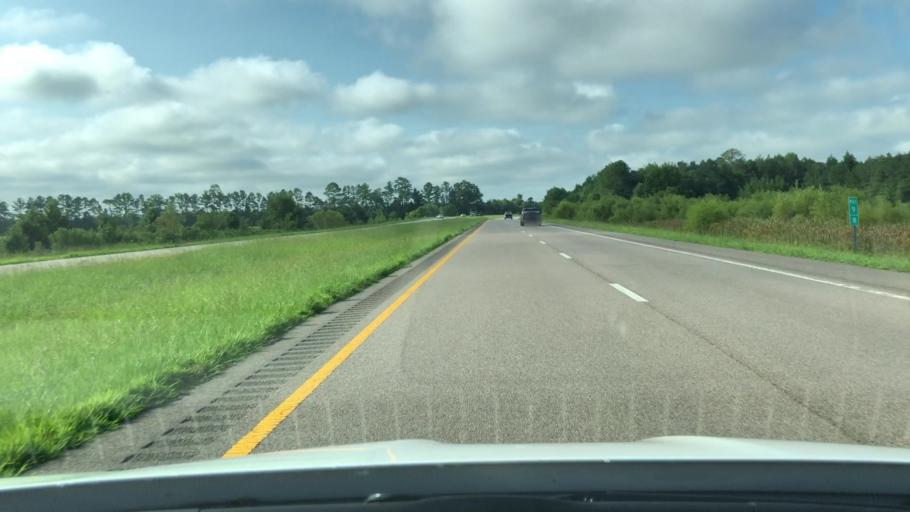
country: US
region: Virginia
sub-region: City of Portsmouth
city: Portsmouth Heights
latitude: 36.6822
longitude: -76.3474
